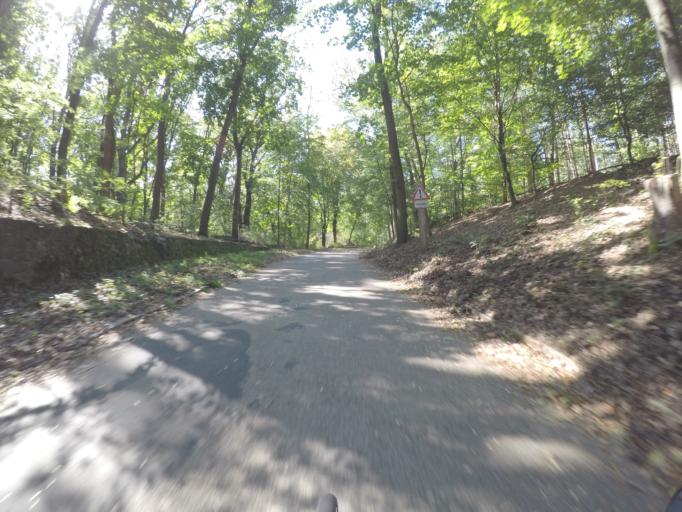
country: DE
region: Berlin
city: Konradshohe
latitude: 52.5837
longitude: 13.2511
